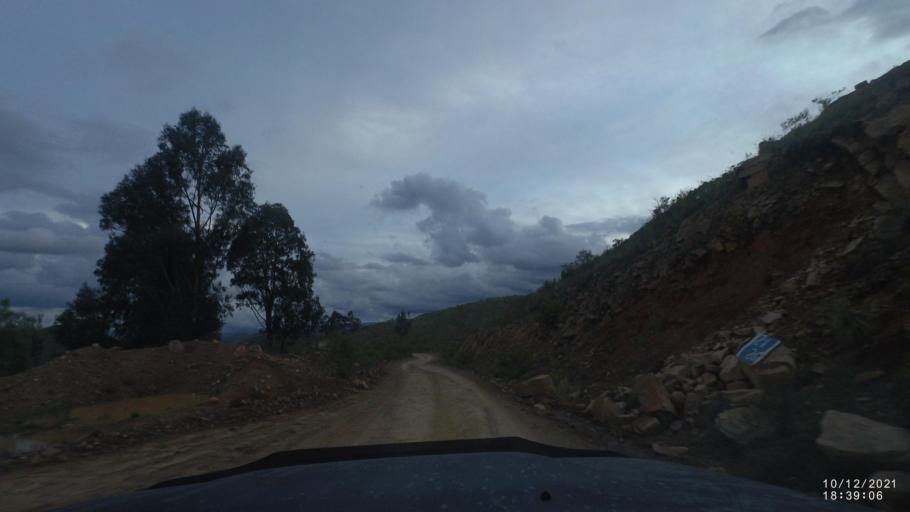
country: BO
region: Cochabamba
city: Tarata
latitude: -17.8474
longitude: -65.9894
